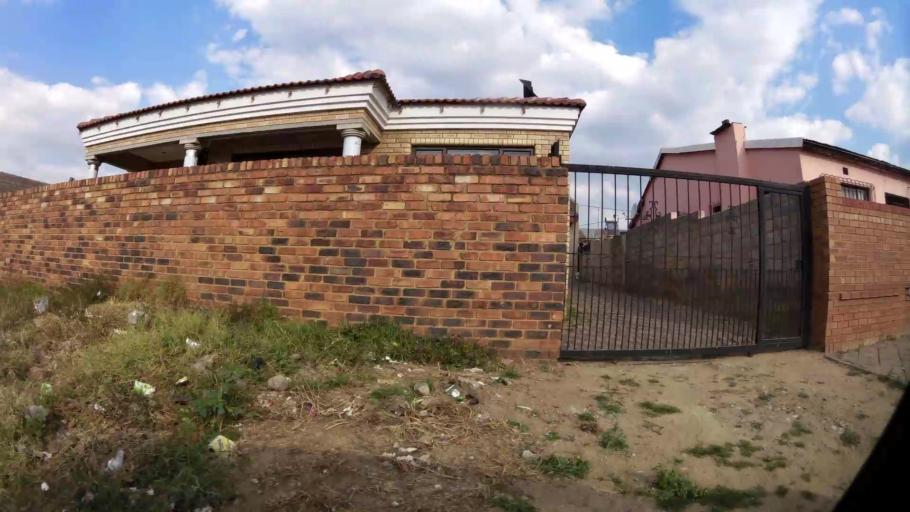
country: ZA
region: Gauteng
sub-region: City of Johannesburg Metropolitan Municipality
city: Soweto
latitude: -26.2256
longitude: 27.9357
